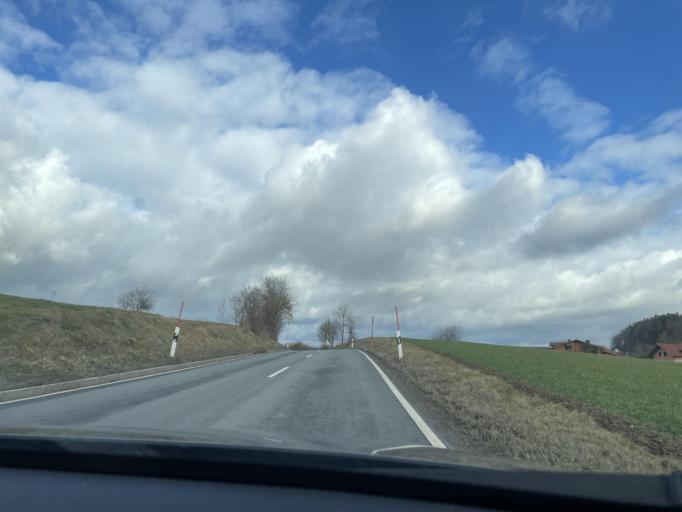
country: DE
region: Bavaria
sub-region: Upper Palatinate
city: Runding
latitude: 49.2107
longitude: 12.7689
